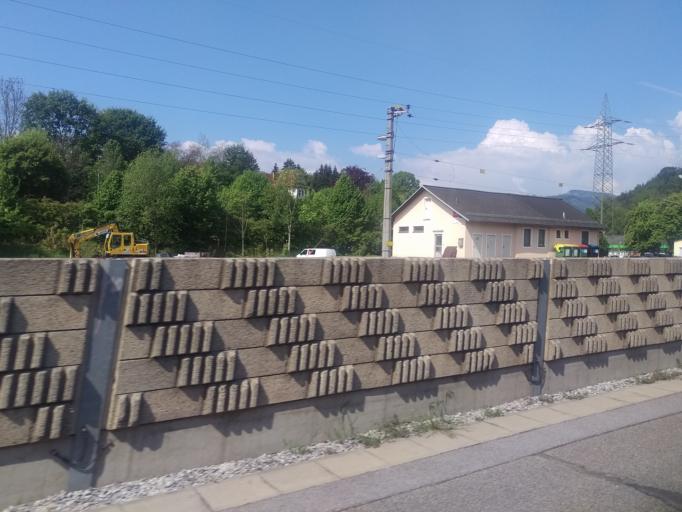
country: AT
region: Styria
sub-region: Politischer Bezirk Graz-Umgebung
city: Gratwein
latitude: 47.1285
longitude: 15.3237
